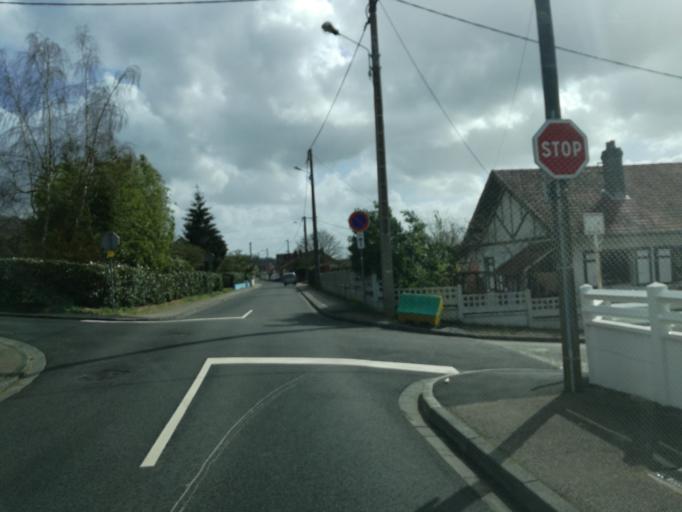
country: FR
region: Haute-Normandie
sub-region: Departement de la Seine-Maritime
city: Le Trait
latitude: 49.4900
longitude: 0.8016
